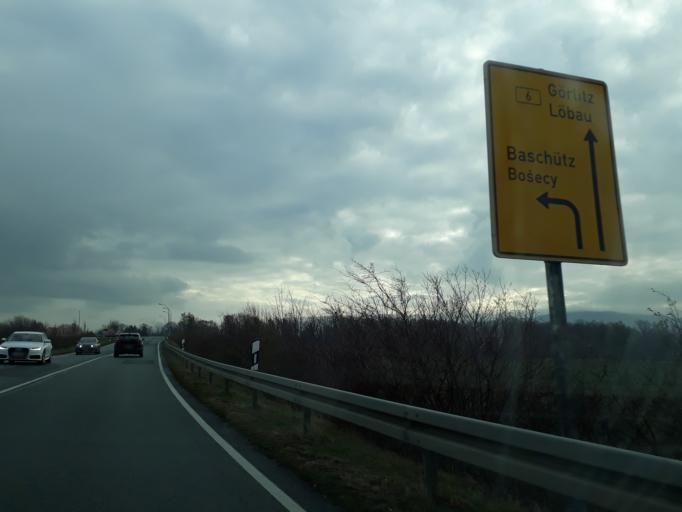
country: DE
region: Saxony
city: Kubschutz
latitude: 51.1651
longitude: 14.5010
